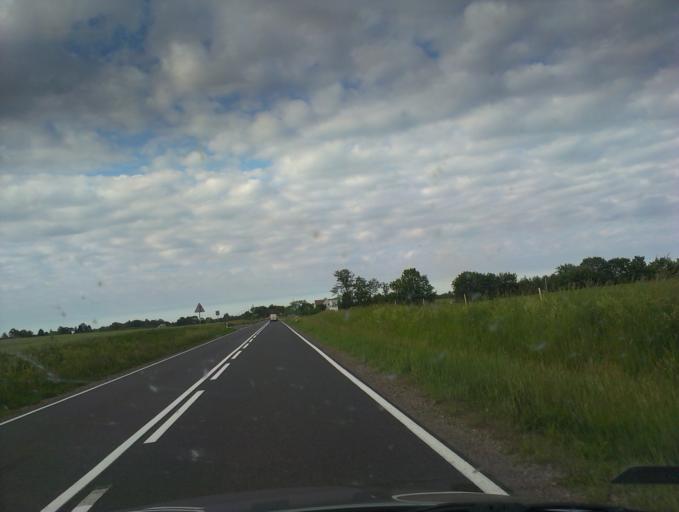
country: PL
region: West Pomeranian Voivodeship
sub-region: Powiat szczecinecki
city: Szczecinek
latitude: 53.6737
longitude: 16.6815
